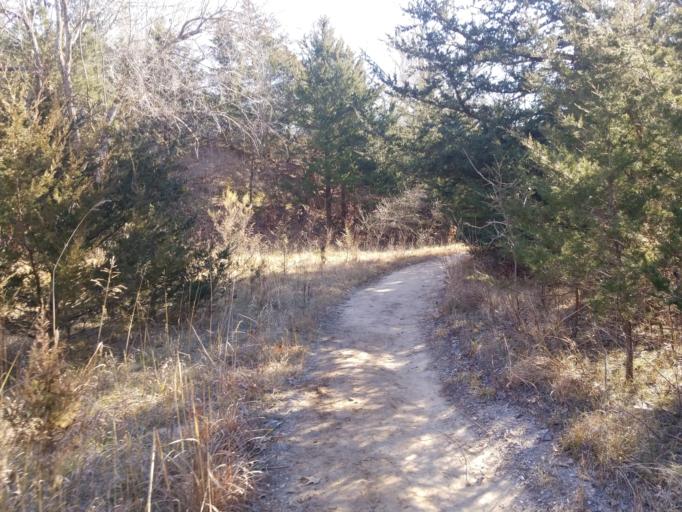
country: US
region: Nebraska
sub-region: Saunders County
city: Ashland
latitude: 41.0144
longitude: -96.2887
